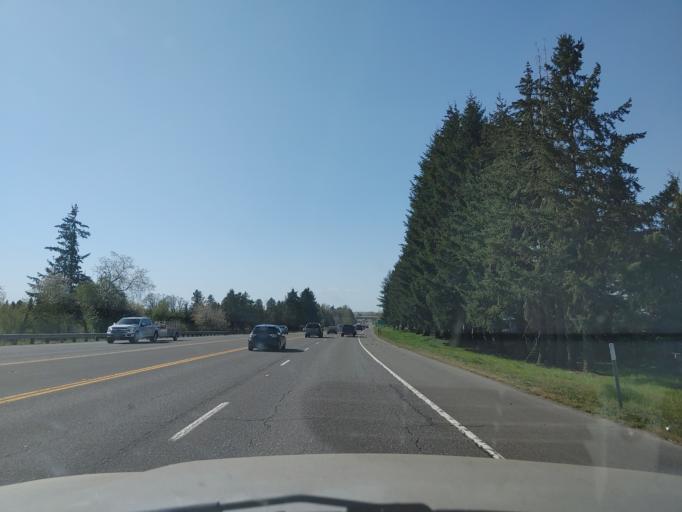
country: US
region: Oregon
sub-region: Clackamas County
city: Oatfield
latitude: 45.4252
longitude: -122.5954
